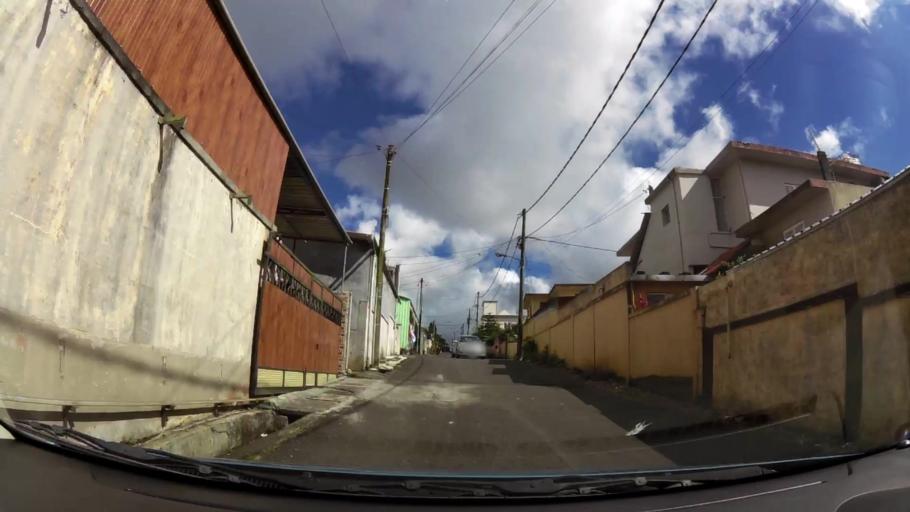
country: MU
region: Plaines Wilhems
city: Curepipe
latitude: -20.3298
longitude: 57.5349
